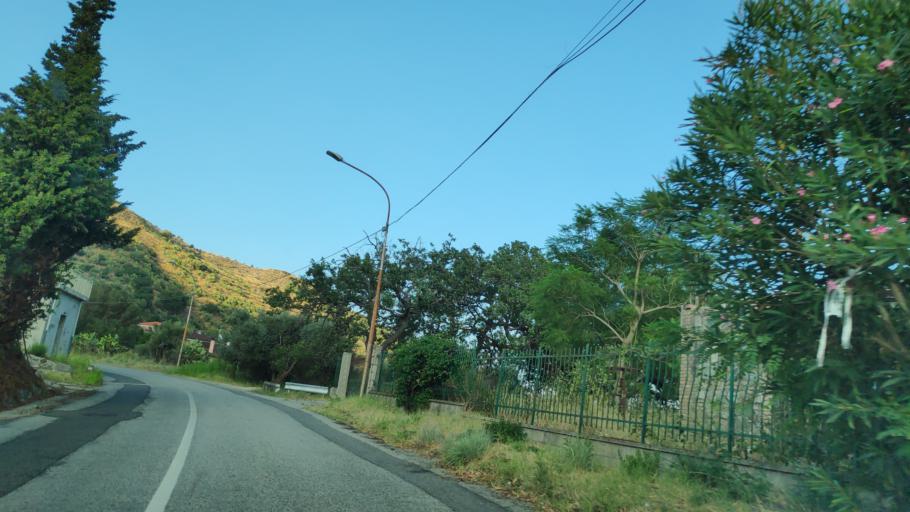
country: IT
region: Calabria
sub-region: Provincia di Catanzaro
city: Satriano
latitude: 38.6742
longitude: 16.4914
